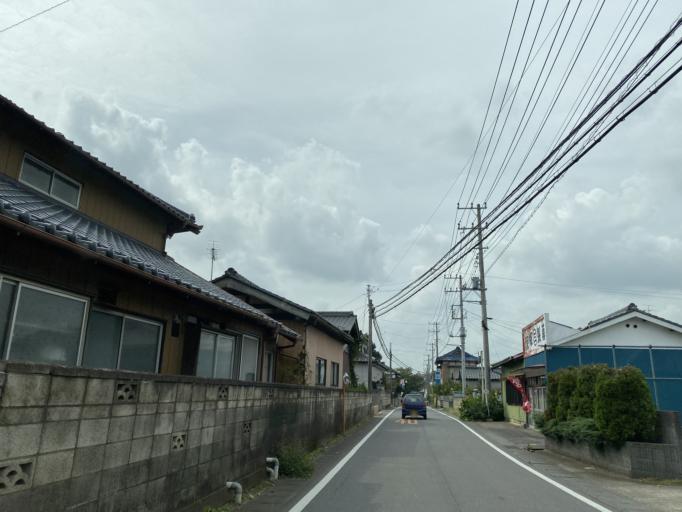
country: JP
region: Ibaraki
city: Mitsukaido
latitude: 36.0424
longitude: 140.0459
